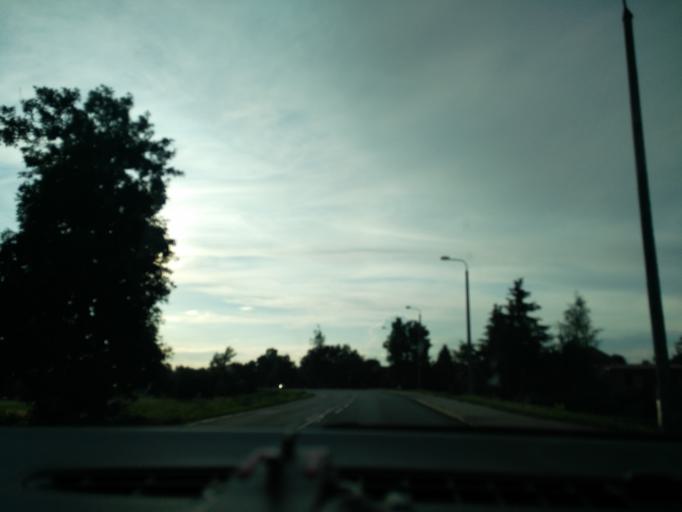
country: PL
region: Lublin Voivodeship
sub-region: Powiat krasnicki
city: Krasnik
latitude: 50.9082
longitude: 22.2644
